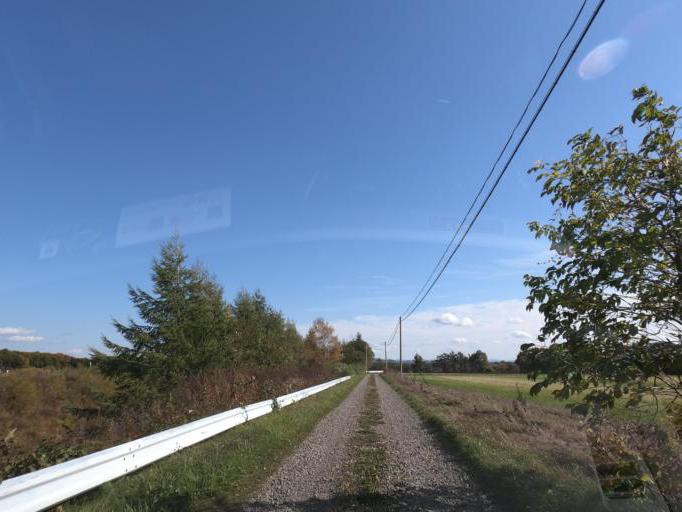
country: JP
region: Hokkaido
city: Otofuke
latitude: 43.2402
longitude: 143.2610
